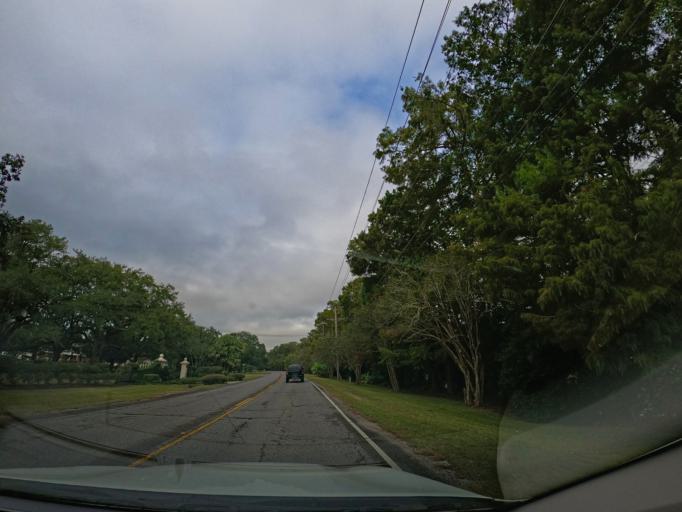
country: US
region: Louisiana
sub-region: Terrebonne Parish
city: Houma
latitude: 29.5764
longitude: -90.7320
